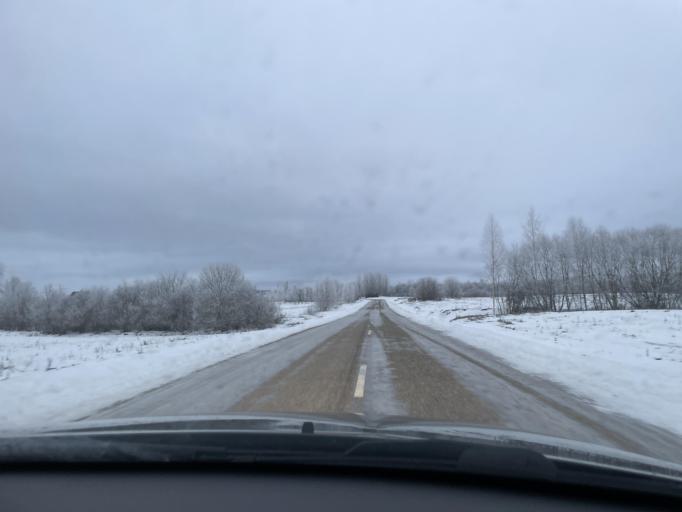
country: LV
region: Ludzas Rajons
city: Ludza
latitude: 56.4572
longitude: 27.5652
